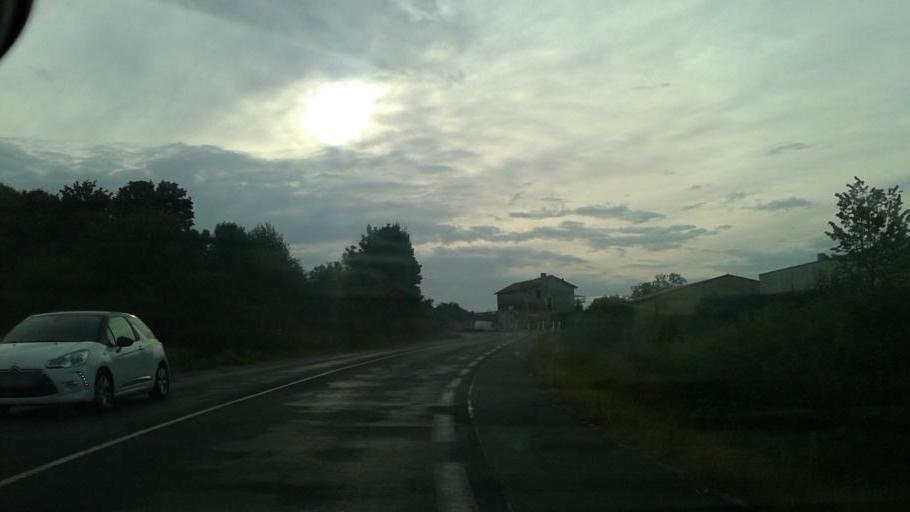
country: FR
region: Rhone-Alpes
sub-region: Departement du Rhone
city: Rillieux-la-Pape
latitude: 45.8245
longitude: 4.9211
